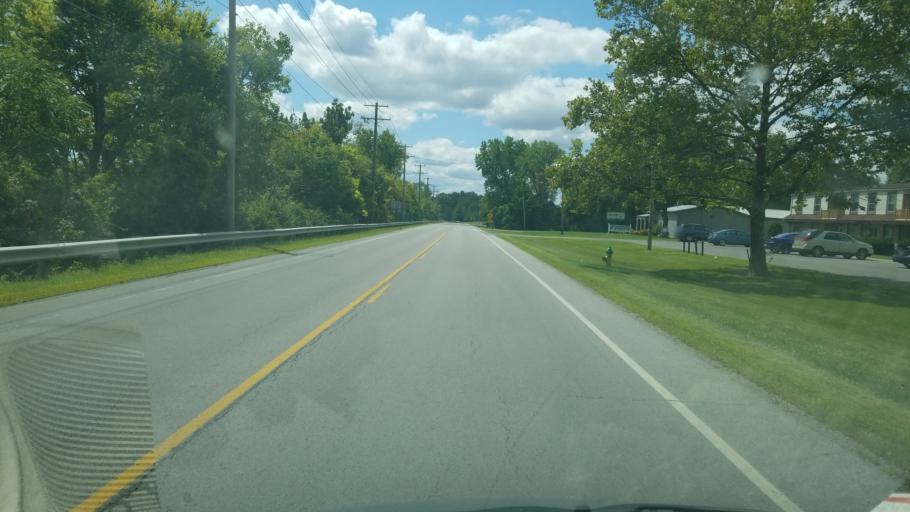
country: US
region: Ohio
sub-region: Henry County
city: Napoleon
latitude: 41.4058
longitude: -84.1054
